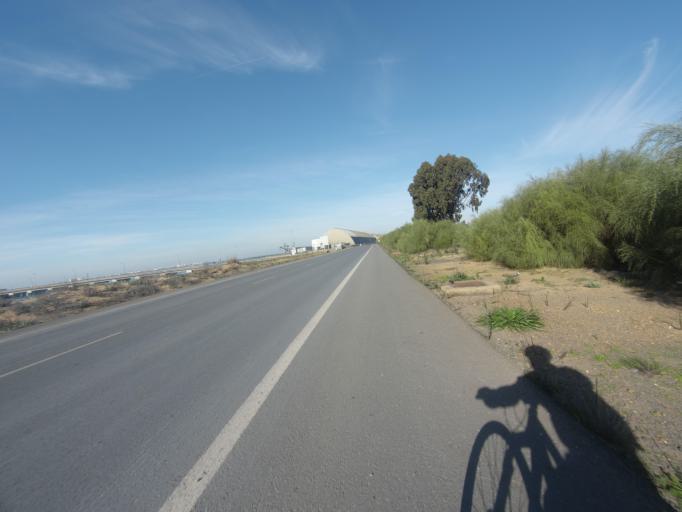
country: ES
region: Andalusia
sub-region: Provincia de Huelva
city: Punta Umbria
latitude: 37.1777
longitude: -6.9175
